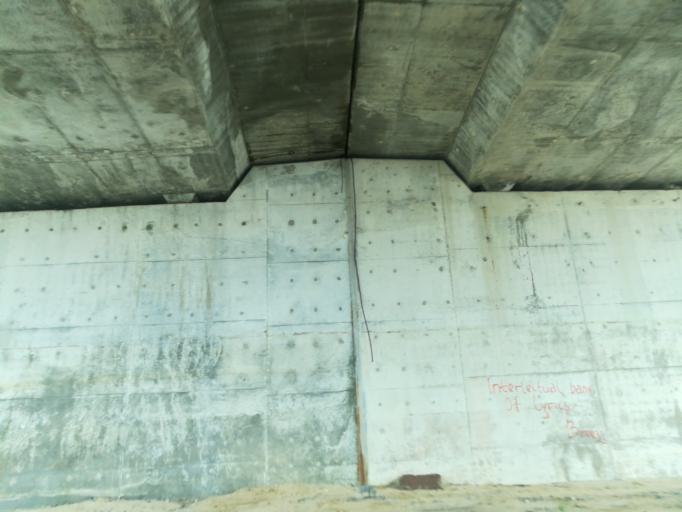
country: NG
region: Lagos
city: Ikoyi
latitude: 6.4128
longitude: 3.4141
